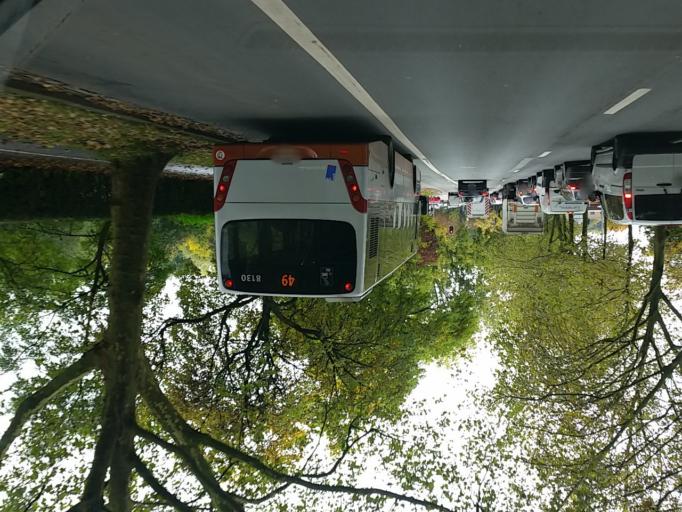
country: BE
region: Flanders
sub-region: Provincie Vlaams-Brabant
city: Drogenbos
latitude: 50.8239
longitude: 4.3116
